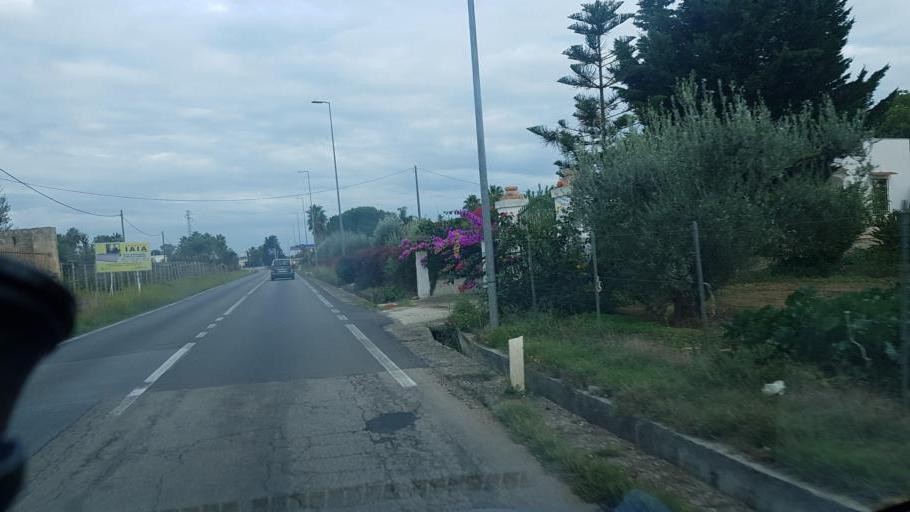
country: IT
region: Apulia
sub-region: Provincia di Brindisi
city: Francavilla Fontana
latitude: 40.5226
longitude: 17.5978
